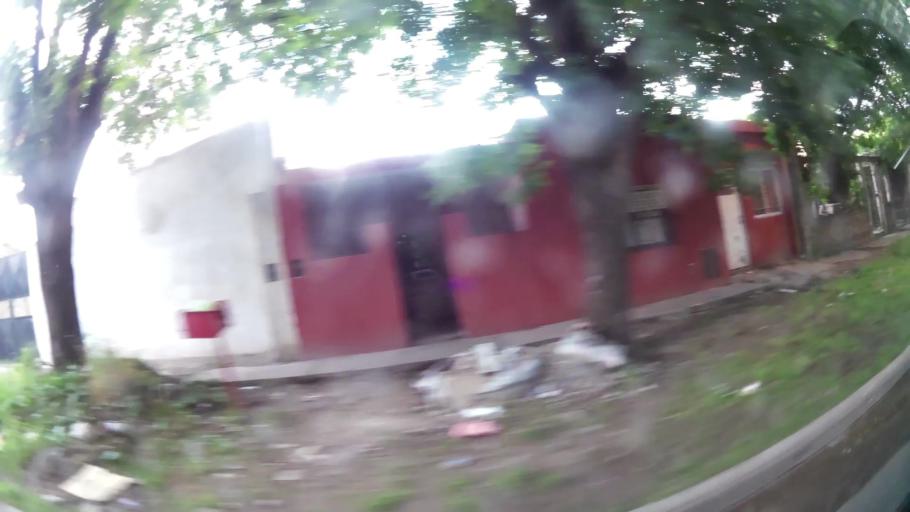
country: AR
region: Buenos Aires
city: San Nicolas de los Arroyos
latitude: -33.3185
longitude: -60.2429
